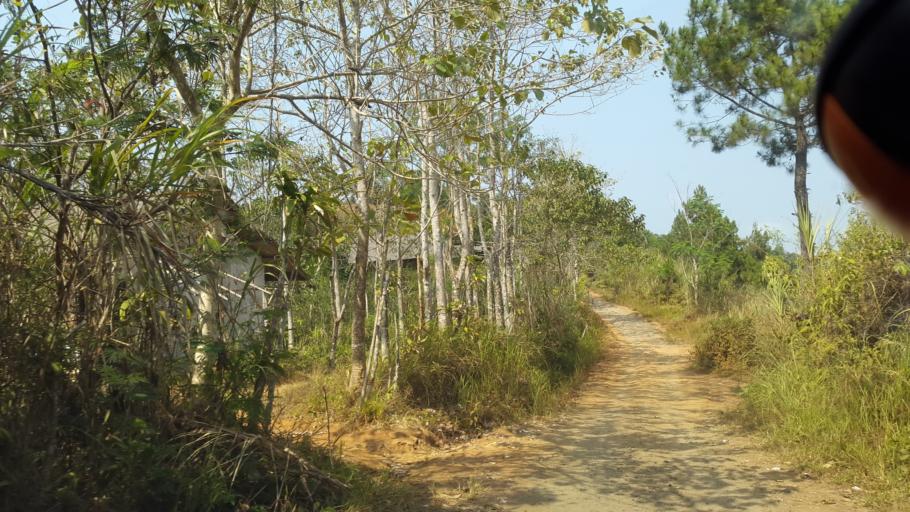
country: ID
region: West Java
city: Sirnasari
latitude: -7.1820
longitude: 106.7687
